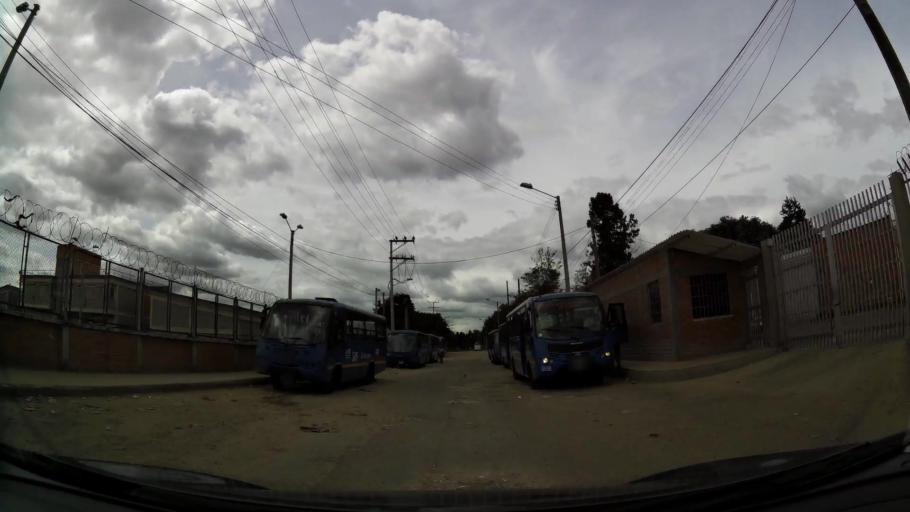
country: CO
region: Cundinamarca
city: Funza
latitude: 4.7181
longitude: -74.1433
